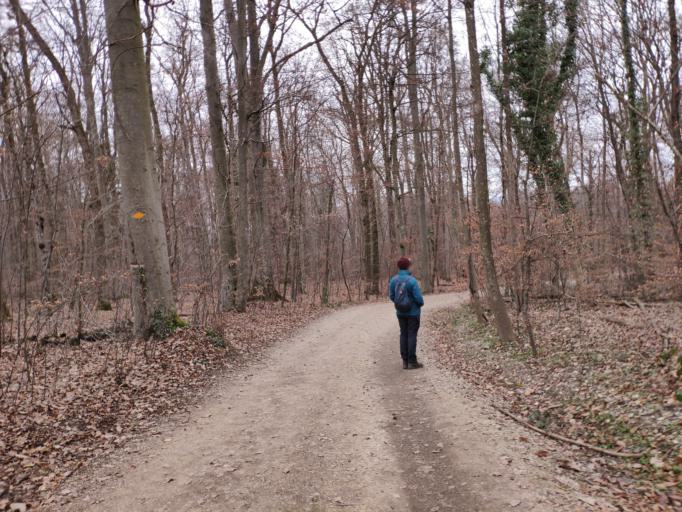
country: CH
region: Basel-City
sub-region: Basel-Stadt
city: Bettingen
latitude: 47.5732
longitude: 7.6779
